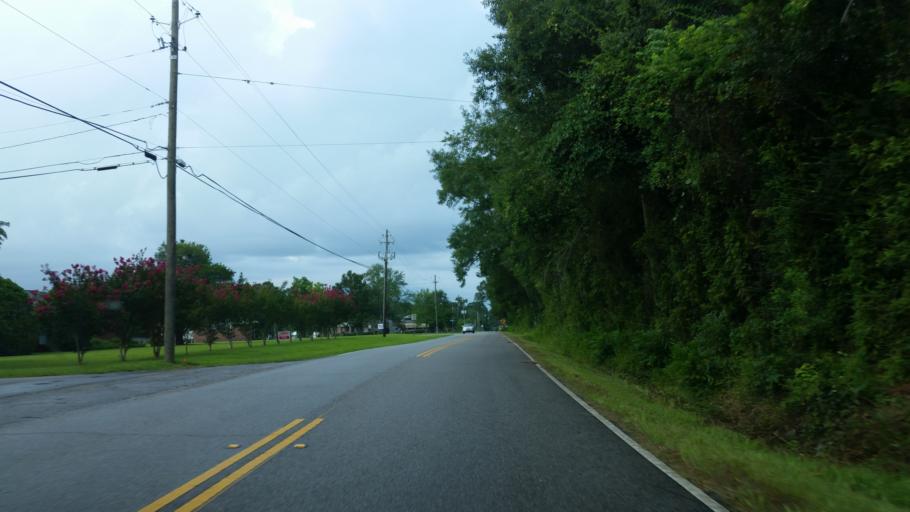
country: US
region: Florida
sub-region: Escambia County
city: Gonzalez
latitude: 30.5729
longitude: -87.2951
